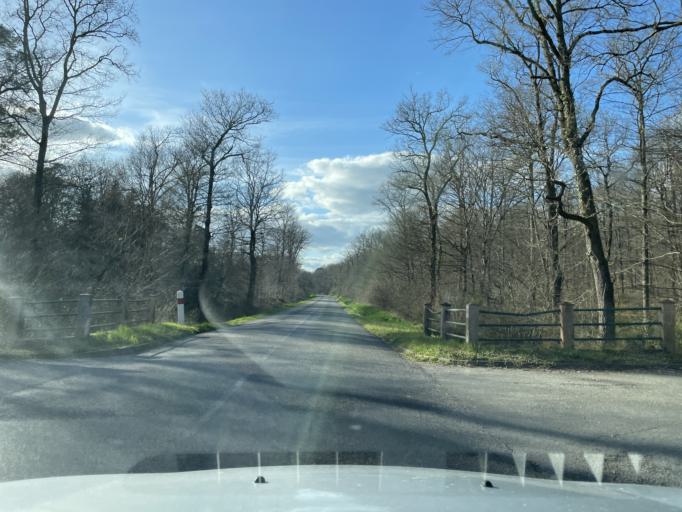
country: FR
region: Midi-Pyrenees
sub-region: Departement de la Haute-Garonne
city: Leguevin
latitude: 43.6152
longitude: 1.2000
